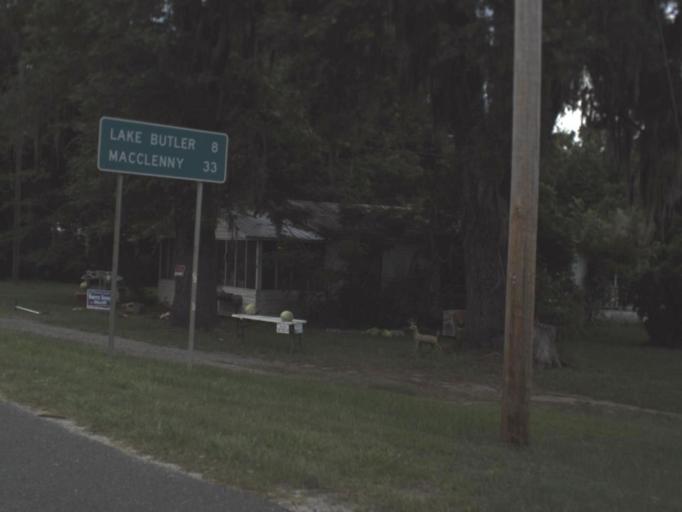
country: US
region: Florida
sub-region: Union County
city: Lake Butler
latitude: 29.9324
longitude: -82.4232
